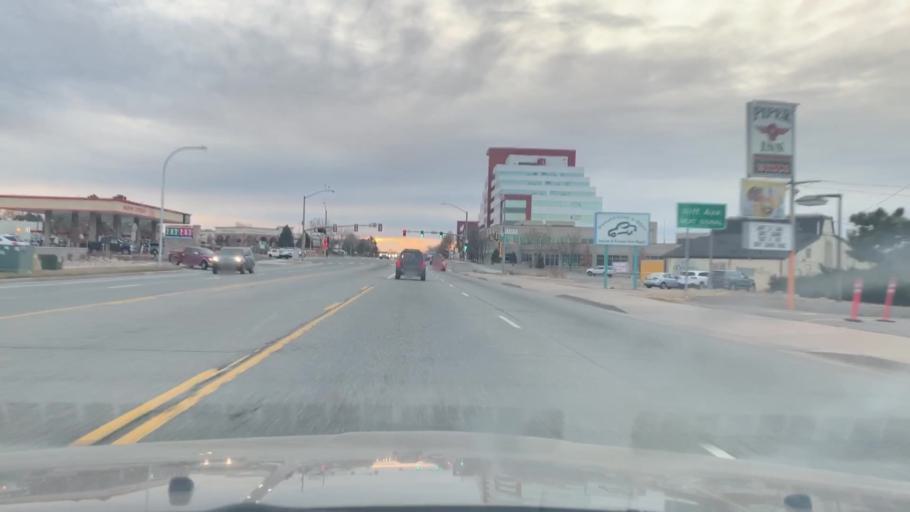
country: US
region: Colorado
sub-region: Adams County
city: Aurora
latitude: 39.6757
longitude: -104.8721
